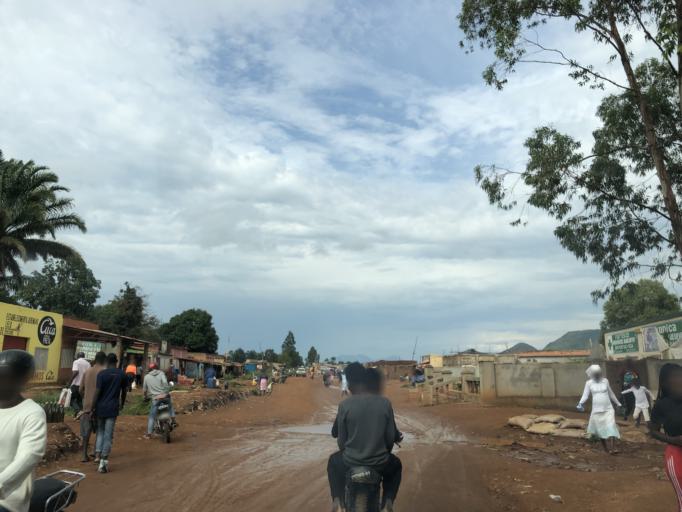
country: AO
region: Cuanza Sul
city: Uacu Cungo
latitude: -11.3485
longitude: 15.0969
